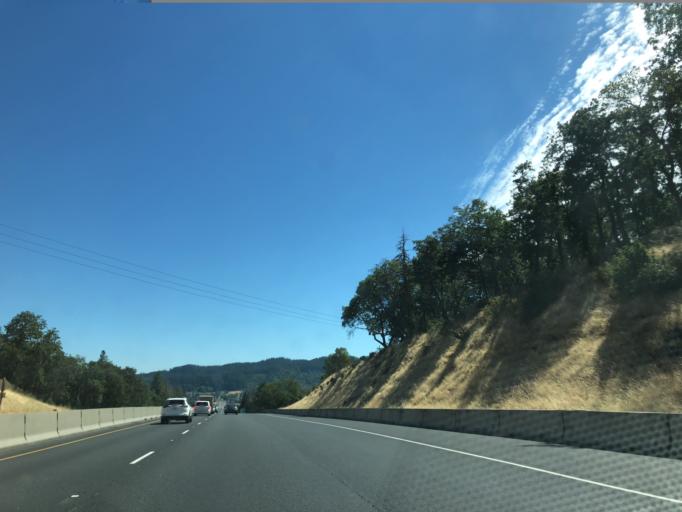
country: US
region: Oregon
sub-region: Douglas County
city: Sutherlin
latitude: 43.4016
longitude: -123.3361
